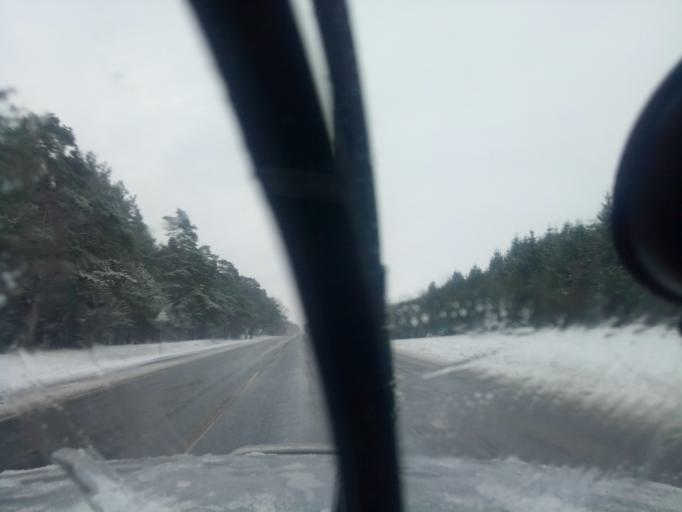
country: BY
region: Minsk
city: Haradzyeya
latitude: 53.2831
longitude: 26.5875
